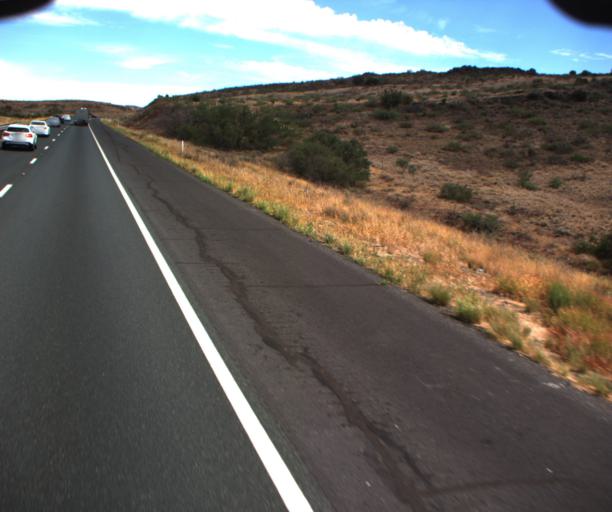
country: US
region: Arizona
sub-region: Yavapai County
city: Cordes Lakes
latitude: 34.4564
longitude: -112.0304
